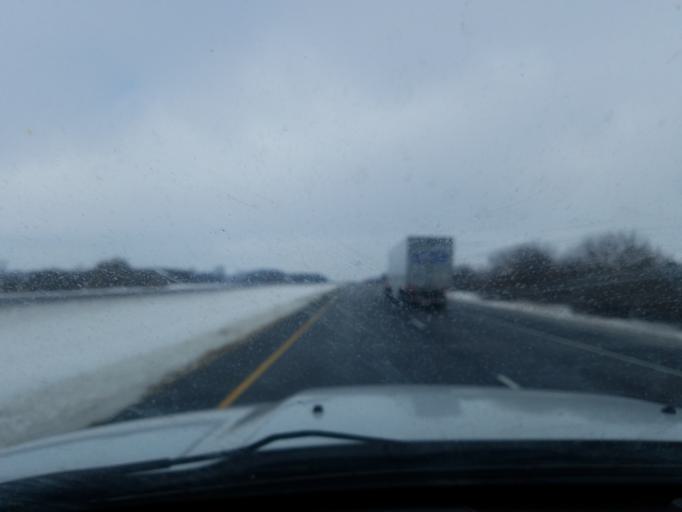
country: US
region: Indiana
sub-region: Marshall County
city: Argos
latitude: 41.2609
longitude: -86.2646
